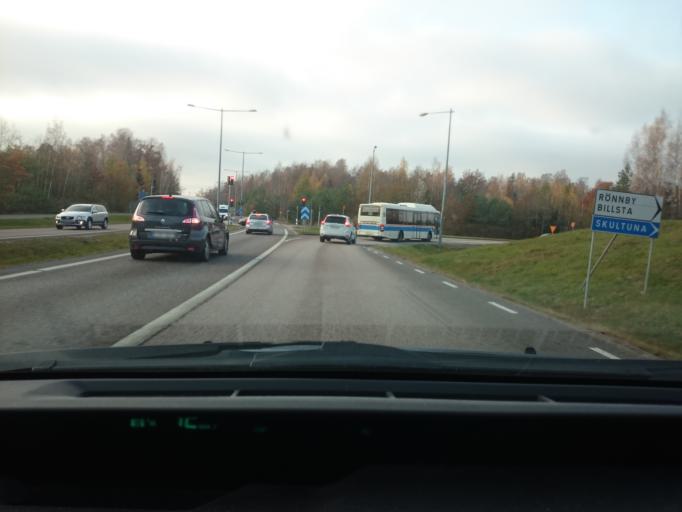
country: SE
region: Vaestmanland
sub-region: Vasteras
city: Vasteras
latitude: 59.6380
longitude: 16.5121
